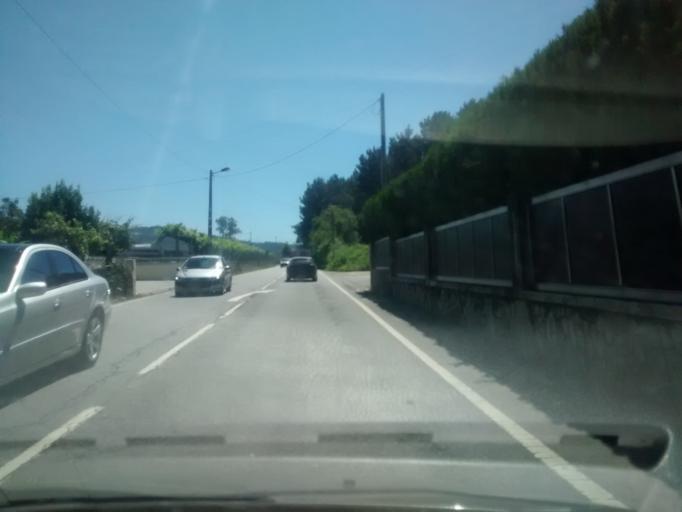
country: PT
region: Braga
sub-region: Barcelos
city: Galegos
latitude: 41.5222
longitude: -8.5683
